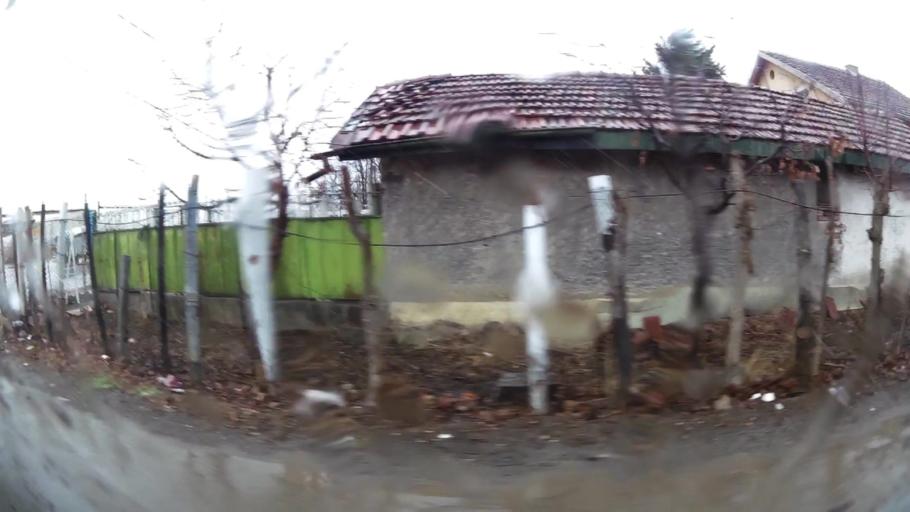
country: BG
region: Sofia-Capital
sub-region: Stolichna Obshtina
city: Sofia
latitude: 42.6634
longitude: 23.4280
